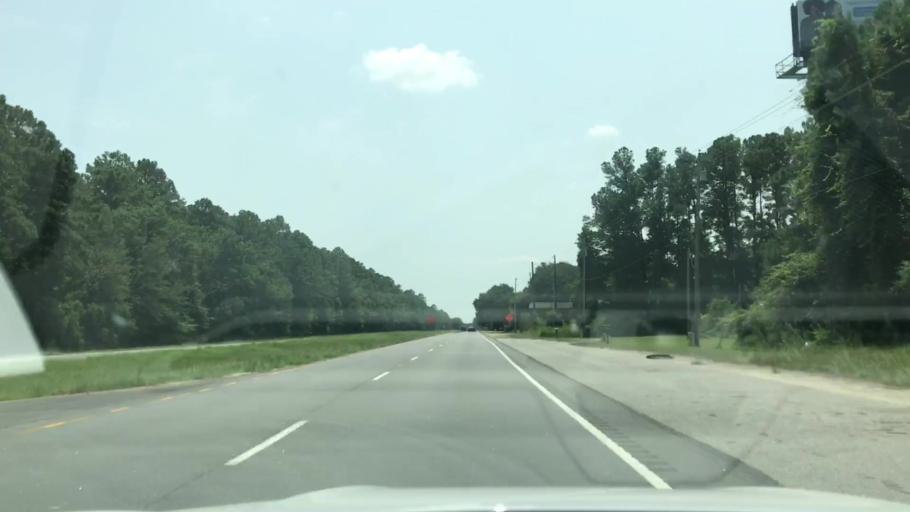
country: US
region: South Carolina
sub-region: Georgetown County
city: Georgetown
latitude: 33.2242
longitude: -79.3783
